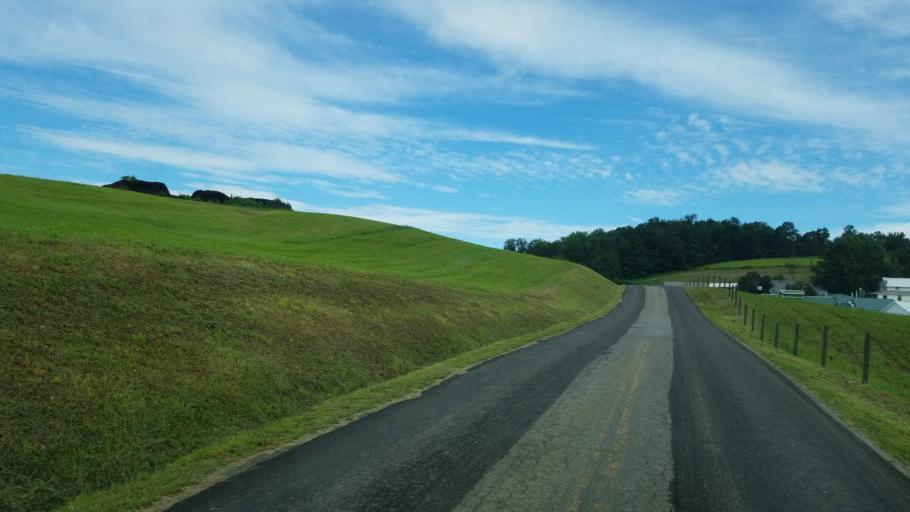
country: US
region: Ohio
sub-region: Holmes County
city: Millersburg
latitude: 40.4932
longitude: -81.8249
